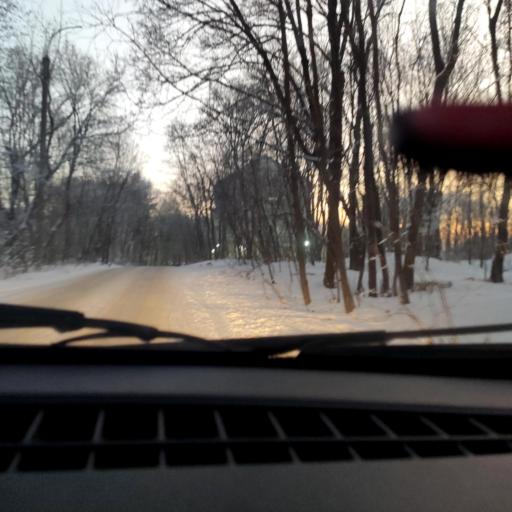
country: RU
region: Bashkortostan
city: Ufa
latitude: 54.7550
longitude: 55.9832
